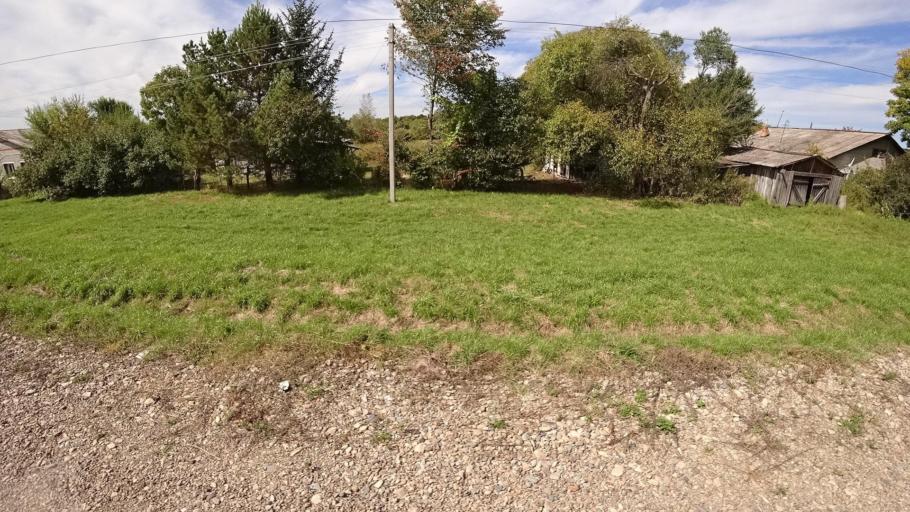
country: RU
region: Primorskiy
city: Yakovlevka
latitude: 44.6421
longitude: 133.6011
